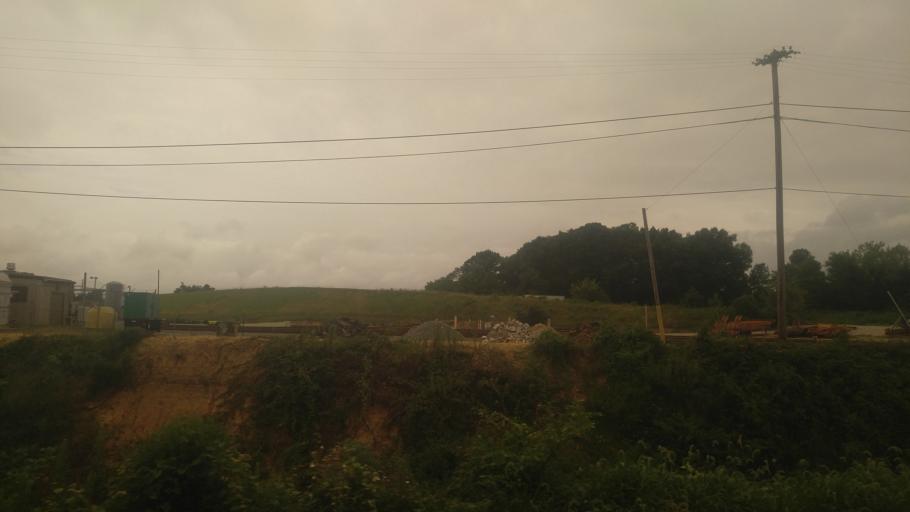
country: US
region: Virginia
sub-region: Henrico County
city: Dumbarton
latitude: 37.5875
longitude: -77.4803
